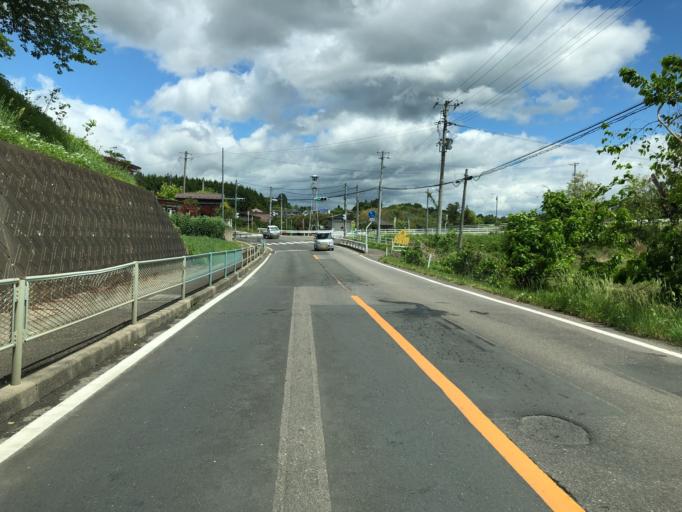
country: JP
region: Fukushima
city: Nihommatsu
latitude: 37.5641
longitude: 140.4563
